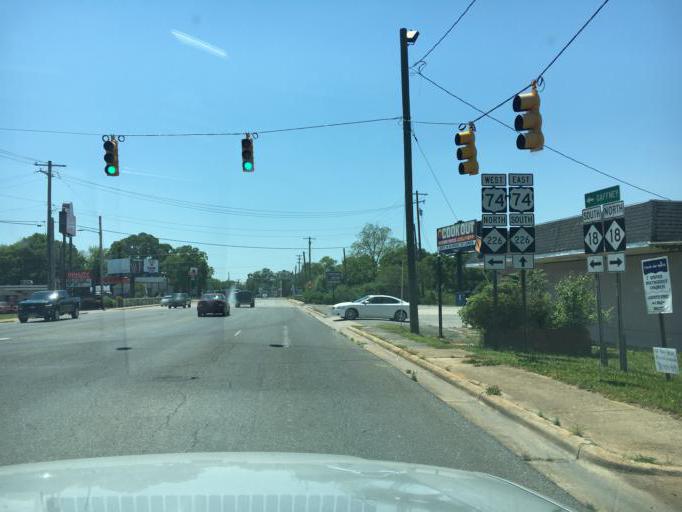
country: US
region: North Carolina
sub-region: Cleveland County
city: Shelby
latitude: 35.2798
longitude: -81.5421
